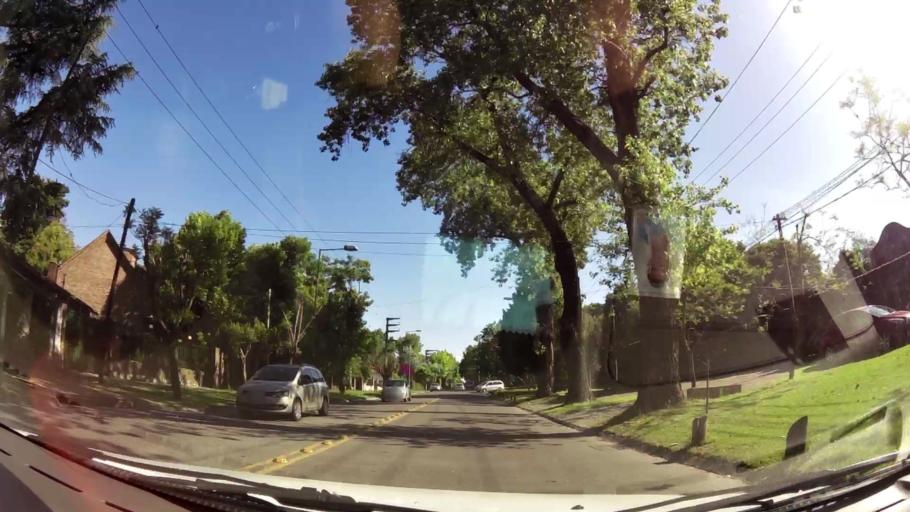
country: AR
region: Buenos Aires
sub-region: Partido de San Isidro
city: San Isidro
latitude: -34.4840
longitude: -58.5560
